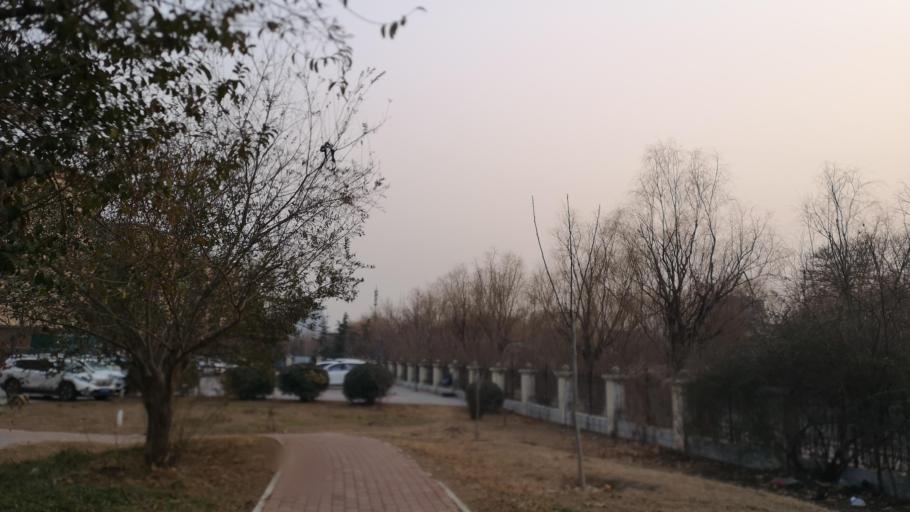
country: CN
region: Henan Sheng
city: Zhongyuanlu
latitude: 35.7883
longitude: 115.0751
